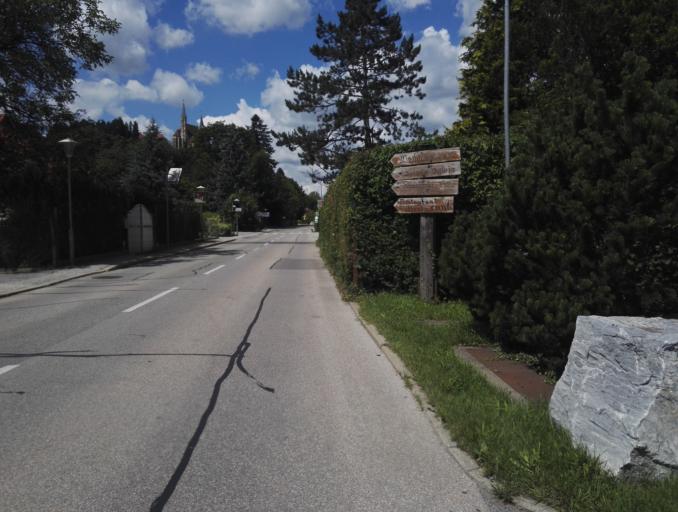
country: AT
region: Styria
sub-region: Politischer Bezirk Graz-Umgebung
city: Gratkorn
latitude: 47.1150
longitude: 15.3454
